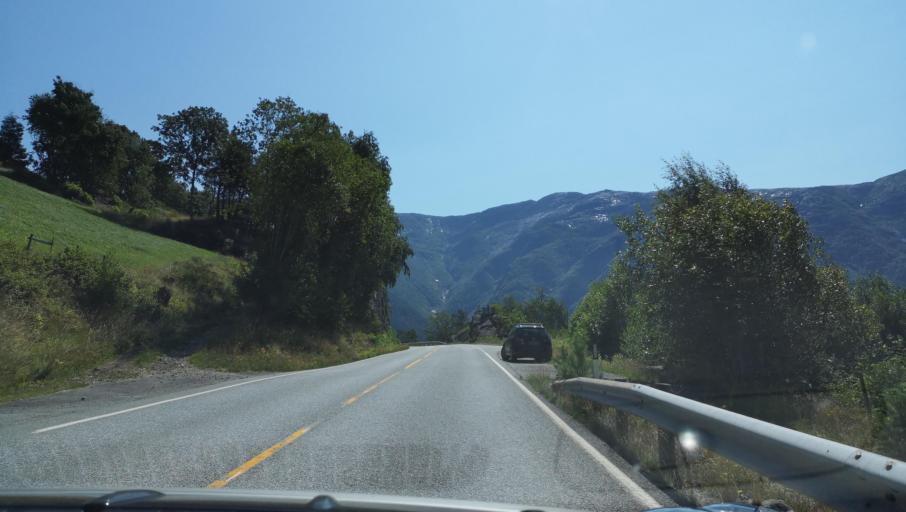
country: NO
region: Hordaland
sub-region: Ulvik
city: Ulvik
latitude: 60.4874
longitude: 6.8722
